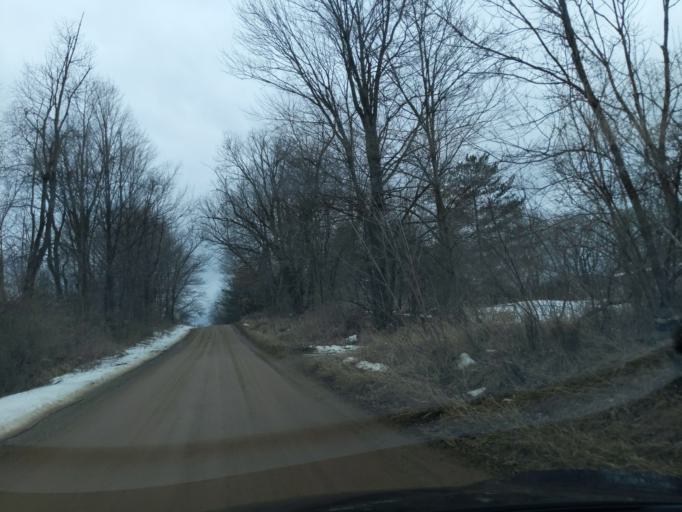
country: US
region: Michigan
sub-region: Eaton County
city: Eaton Rapids
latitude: 42.5386
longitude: -84.6053
